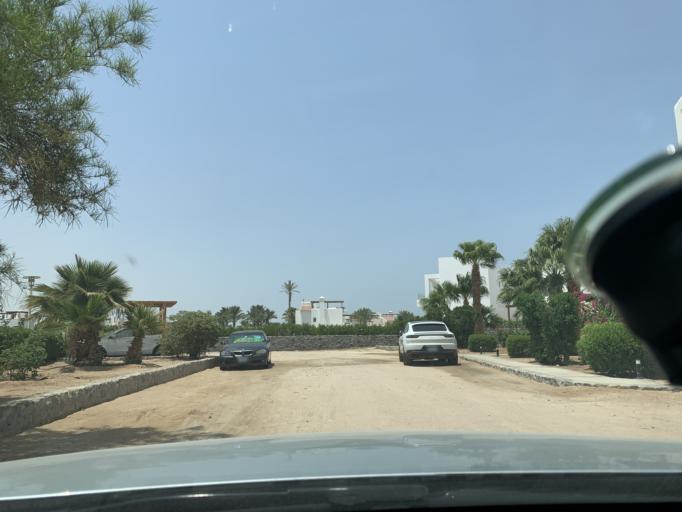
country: EG
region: Red Sea
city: El Gouna
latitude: 27.3692
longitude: 33.6711
